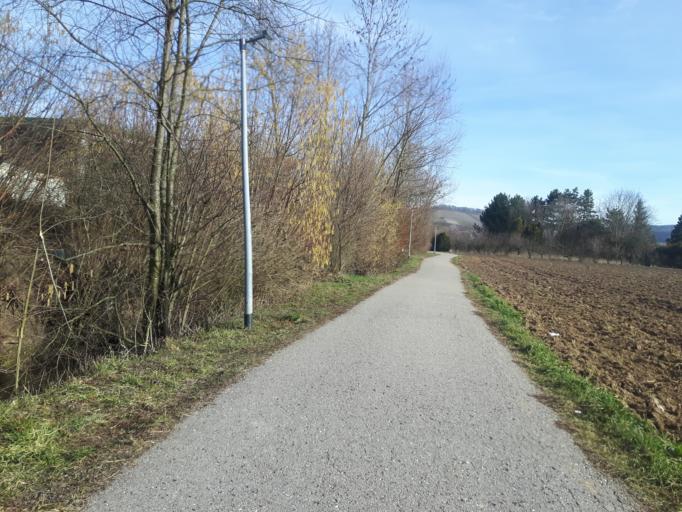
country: DE
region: Baden-Wuerttemberg
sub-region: Regierungsbezirk Stuttgart
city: Lehrensteinsfeld
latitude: 49.1351
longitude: 9.3763
